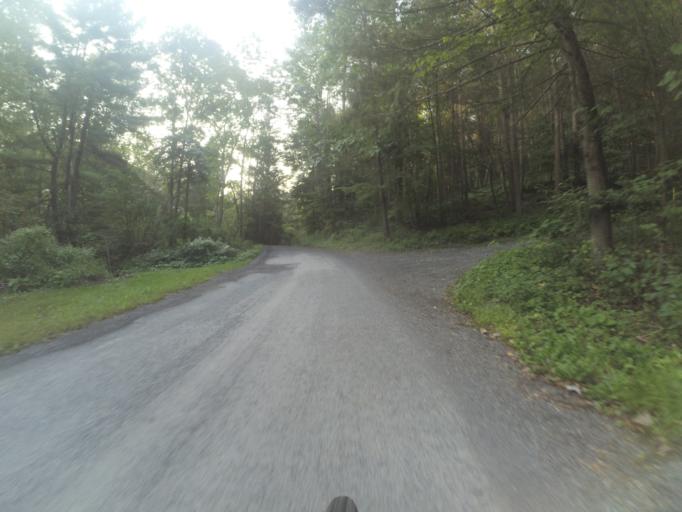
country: US
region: Pennsylvania
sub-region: Mifflin County
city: Milroy
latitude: 40.8533
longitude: -77.4587
